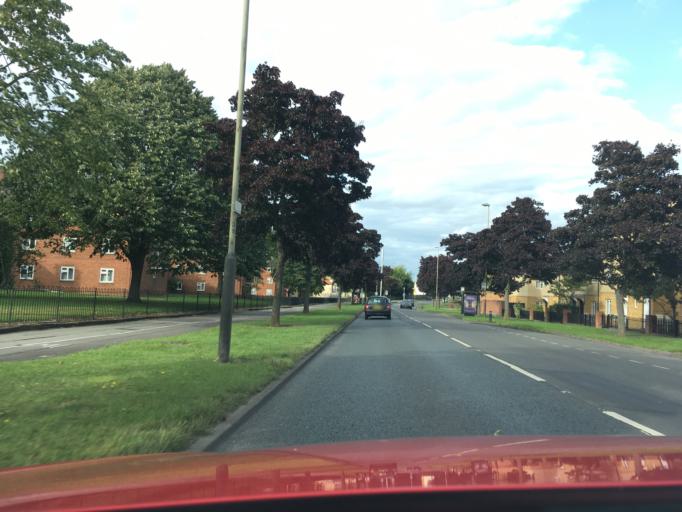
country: GB
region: England
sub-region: Gloucestershire
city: Uckington
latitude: 51.9076
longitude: -2.1125
